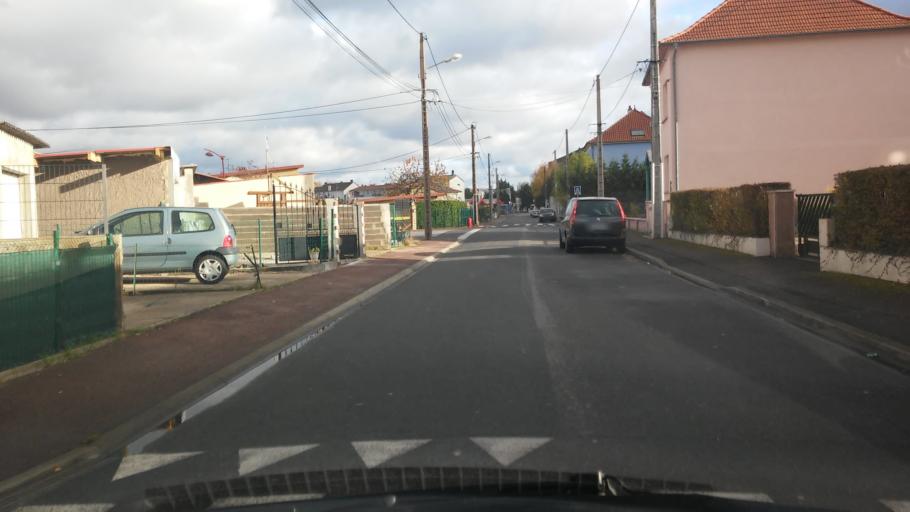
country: FR
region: Lorraine
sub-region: Departement de la Moselle
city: Talange
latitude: 49.2415
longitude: 6.1668
